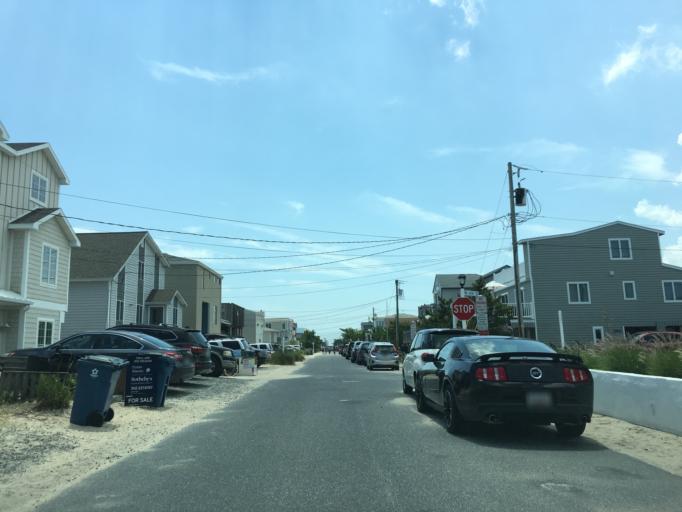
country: US
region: Delaware
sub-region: Sussex County
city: Bethany Beach
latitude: 38.5179
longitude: -75.0535
